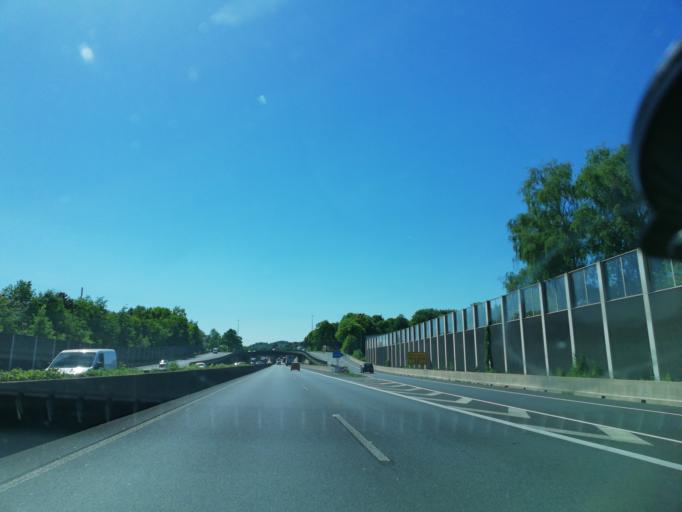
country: DE
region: North Rhine-Westphalia
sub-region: Regierungsbezirk Dusseldorf
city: Wuppertal
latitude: 51.2714
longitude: 7.1589
